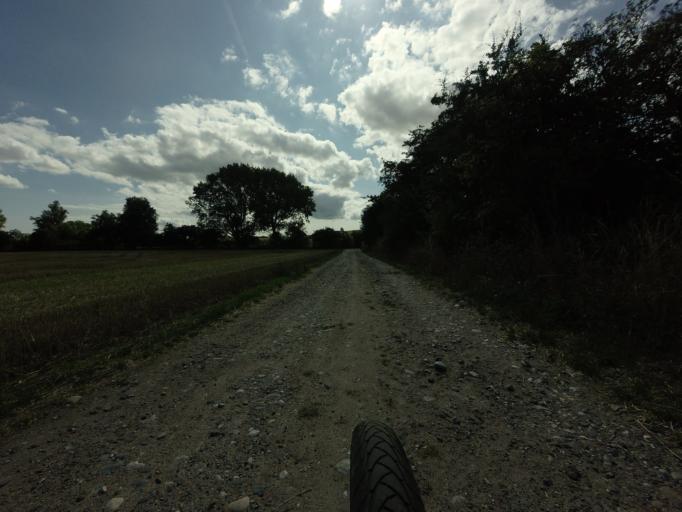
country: DK
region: Zealand
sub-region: Vordingborg Kommune
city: Stege
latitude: 55.0165
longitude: 12.4272
